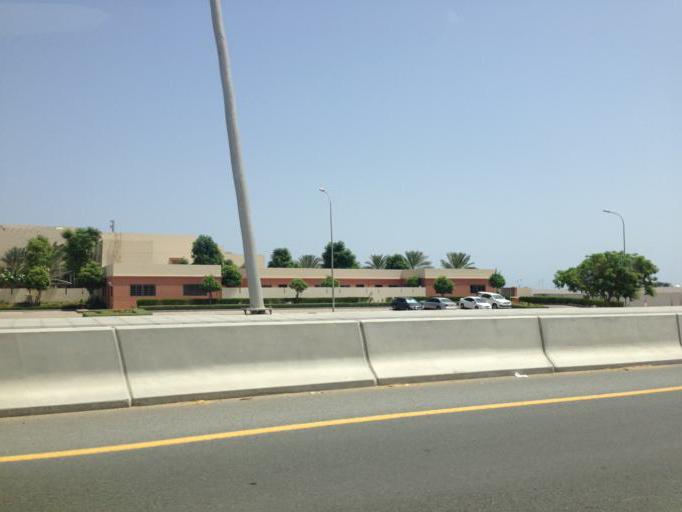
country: OM
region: Muhafazat Masqat
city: Bawshar
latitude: 23.6029
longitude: 58.3417
